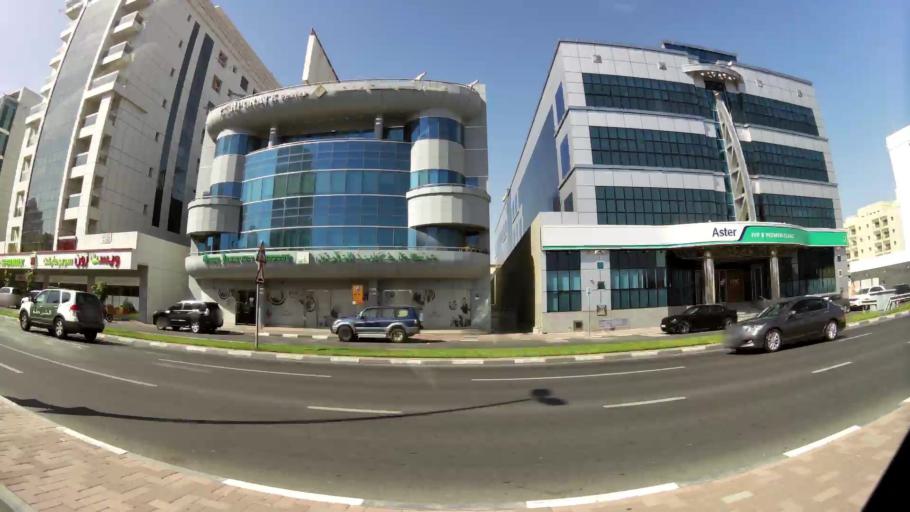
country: AE
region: Ash Shariqah
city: Sharjah
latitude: 25.2528
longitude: 55.2870
